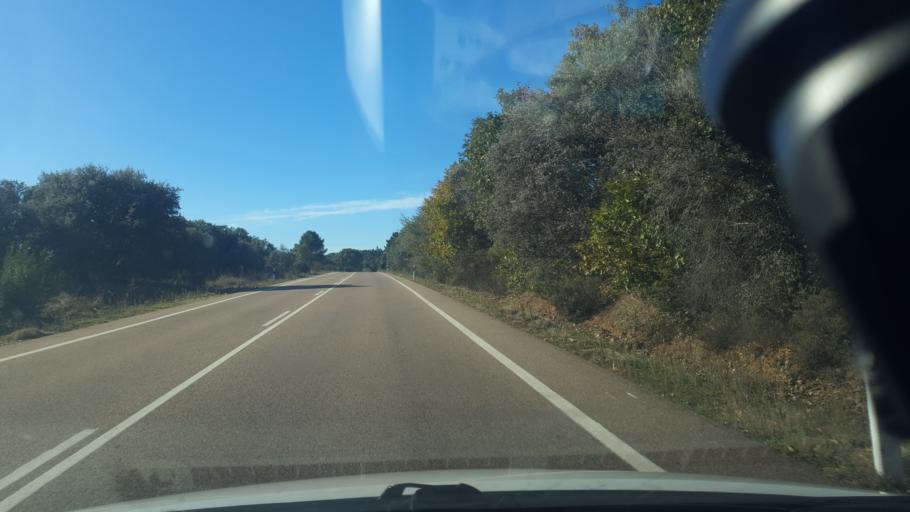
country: ES
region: Castille and Leon
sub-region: Provincia de Avila
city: Arenas de San Pedro
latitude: 40.1726
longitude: -5.0953
